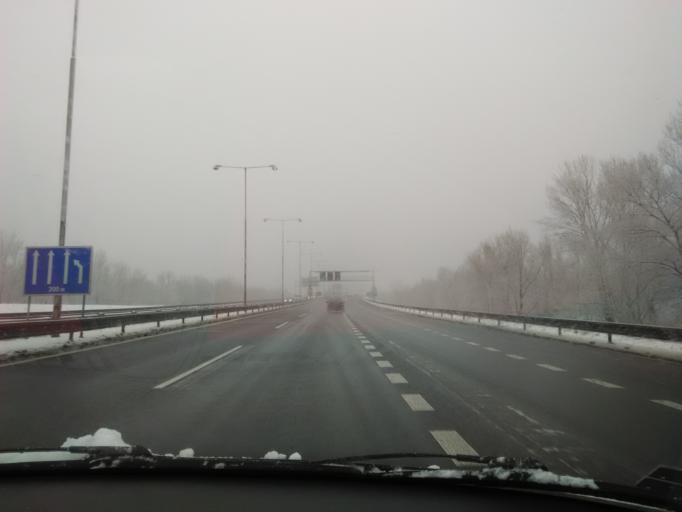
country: SK
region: Bratislavsky
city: Bratislava
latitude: 48.1330
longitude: 17.0745
